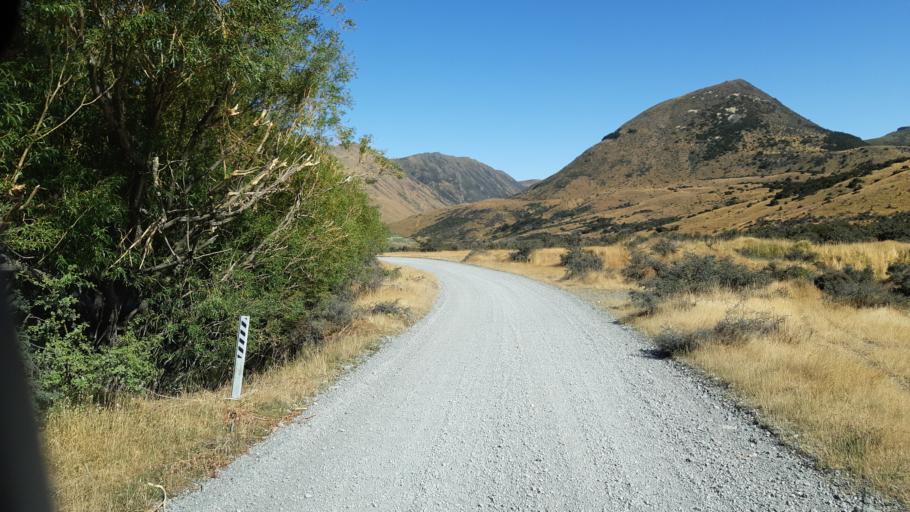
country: NZ
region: Canterbury
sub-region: Ashburton District
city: Methven
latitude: -43.3415
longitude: 171.6110
